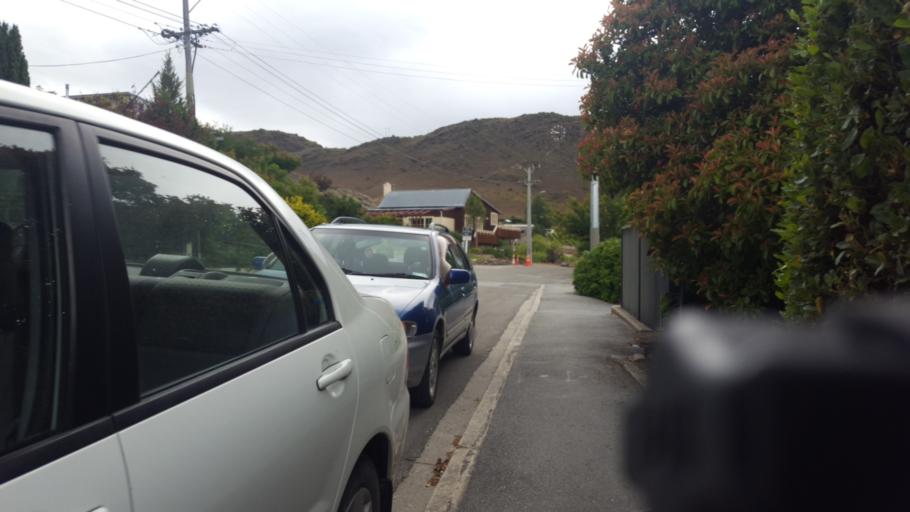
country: NZ
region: Otago
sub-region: Queenstown-Lakes District
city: Wanaka
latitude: -45.2532
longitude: 169.3978
